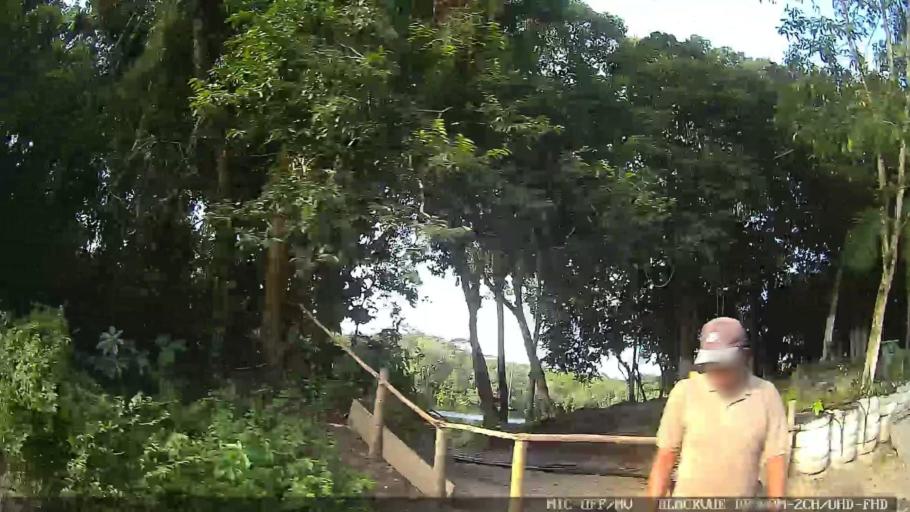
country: BR
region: Sao Paulo
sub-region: Itanhaem
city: Itanhaem
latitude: -24.1497
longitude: -46.8176
